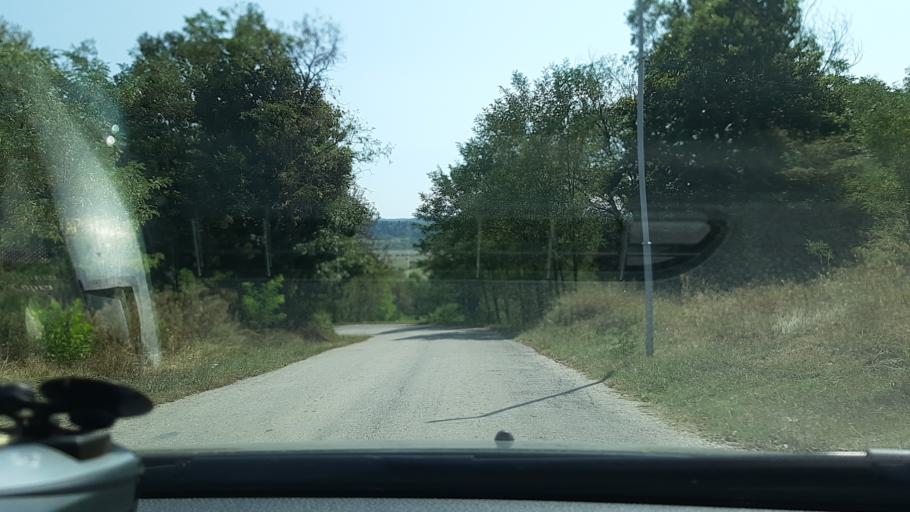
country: RO
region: Gorj
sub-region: Comuna Targu Carbunesti
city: Targu Carbunesti
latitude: 44.9631
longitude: 23.5191
